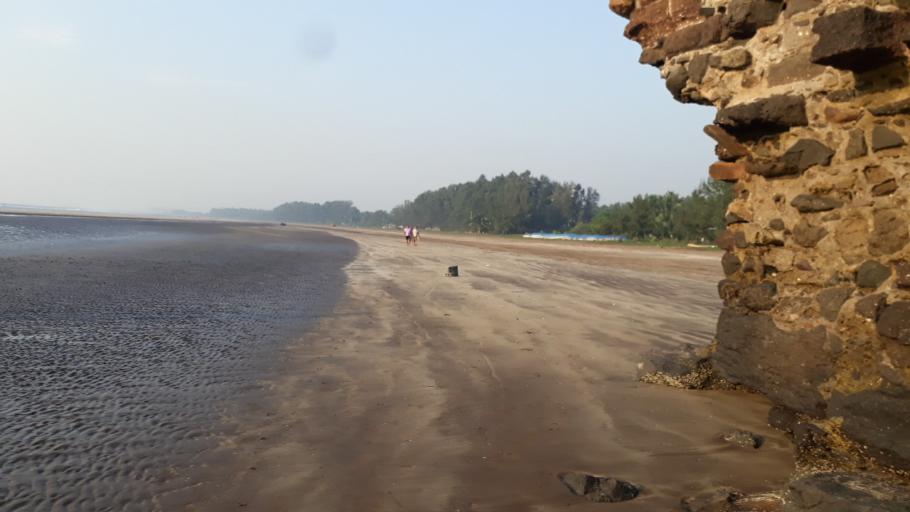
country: IN
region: Maharashtra
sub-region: Raigarh
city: Revadanda
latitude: 18.5475
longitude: 72.9239
